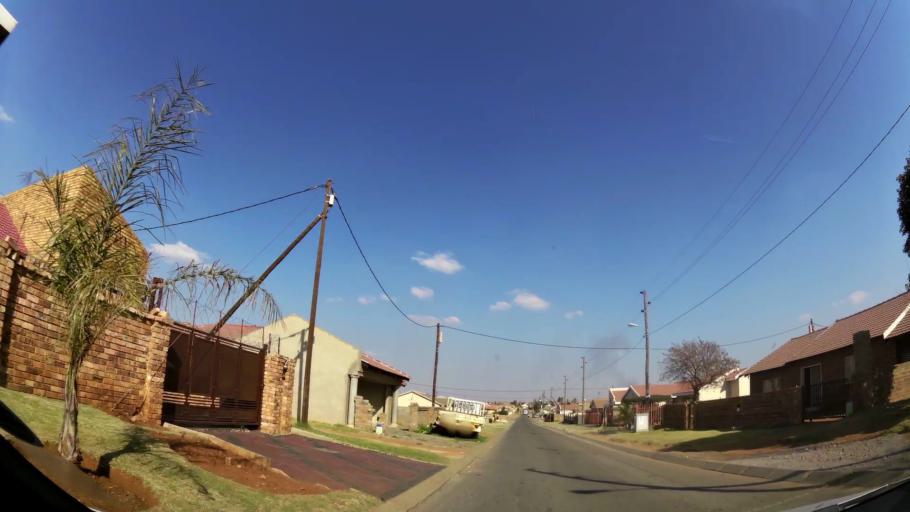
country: ZA
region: Gauteng
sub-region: Ekurhuleni Metropolitan Municipality
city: Benoni
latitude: -26.2226
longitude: 28.3248
